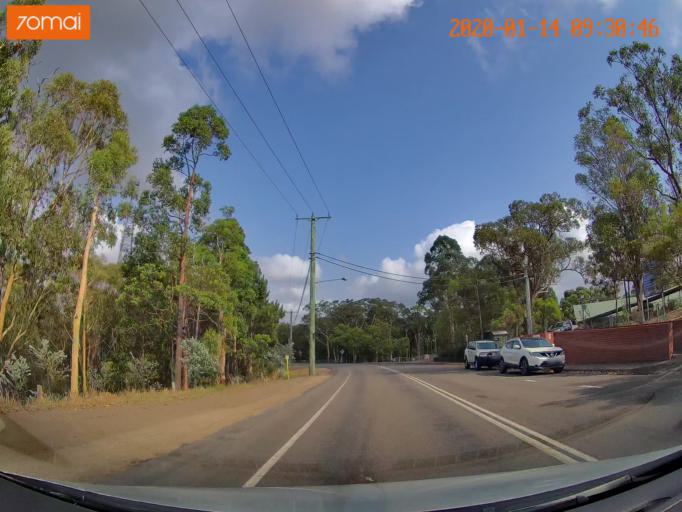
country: AU
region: New South Wales
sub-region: Lake Macquarie Shire
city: Dora Creek
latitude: -33.1145
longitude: 151.5161
